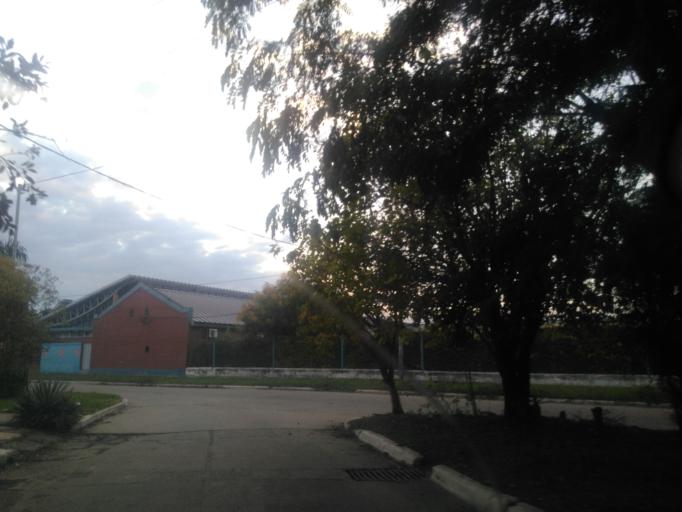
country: AR
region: Chaco
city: Resistencia
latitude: -27.4571
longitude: -59.0166
